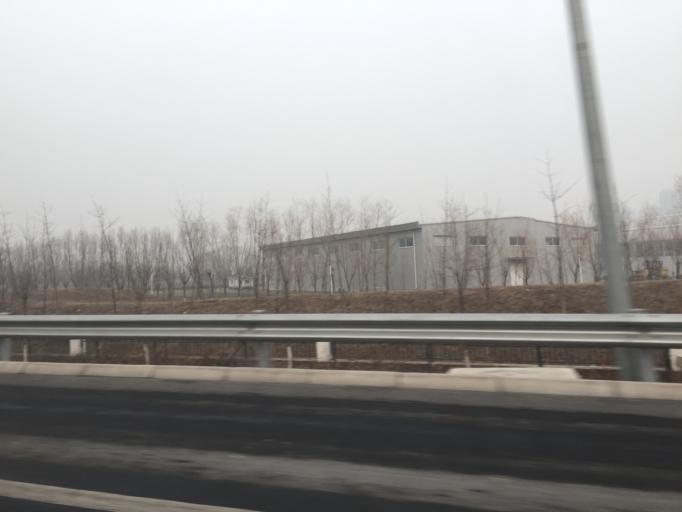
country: CN
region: Beijing
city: Qinghe
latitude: 40.0116
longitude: 116.3276
